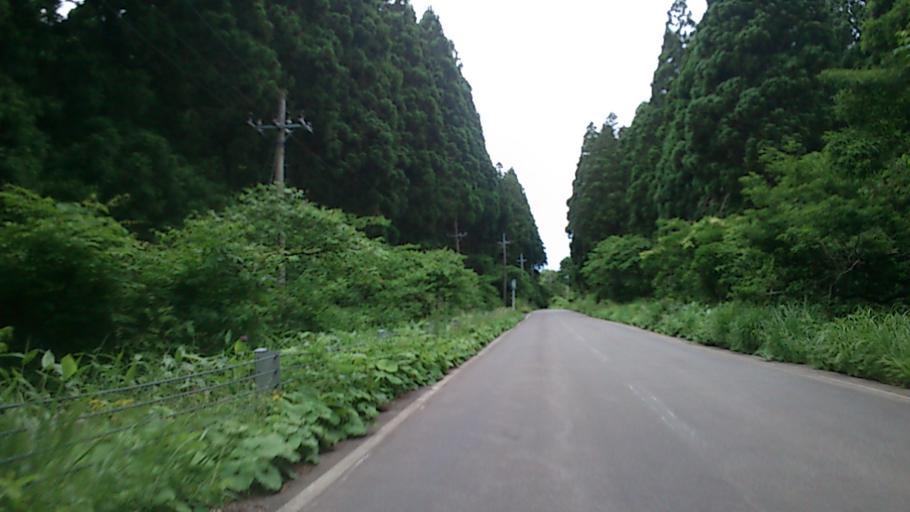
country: JP
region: Yamagata
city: Yuza
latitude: 39.0946
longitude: 139.9163
